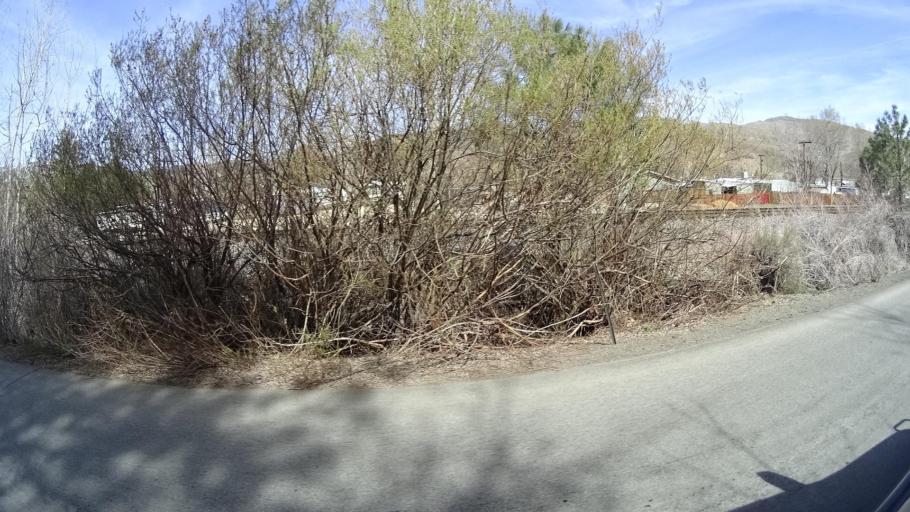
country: US
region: Nevada
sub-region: Washoe County
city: Verdi
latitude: 39.5184
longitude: -119.9857
